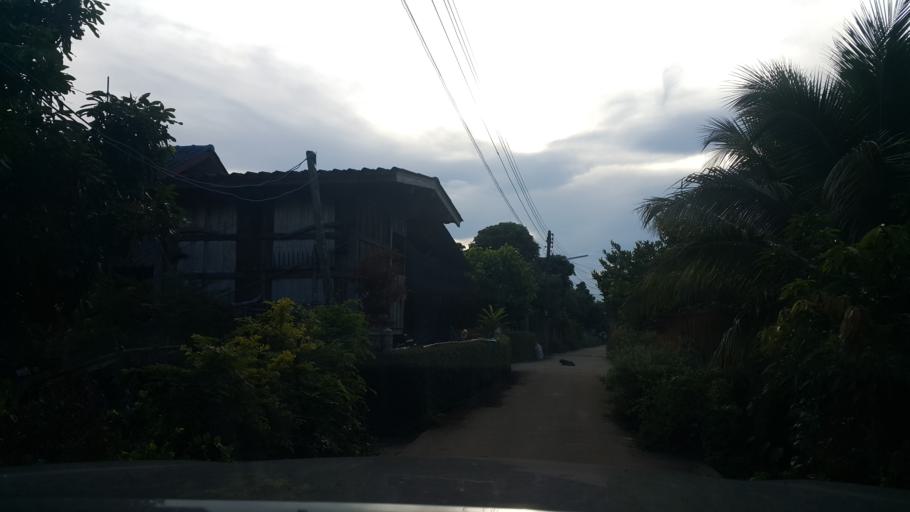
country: TH
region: Chiang Mai
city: Mae Taeng
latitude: 19.1571
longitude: 99.0120
